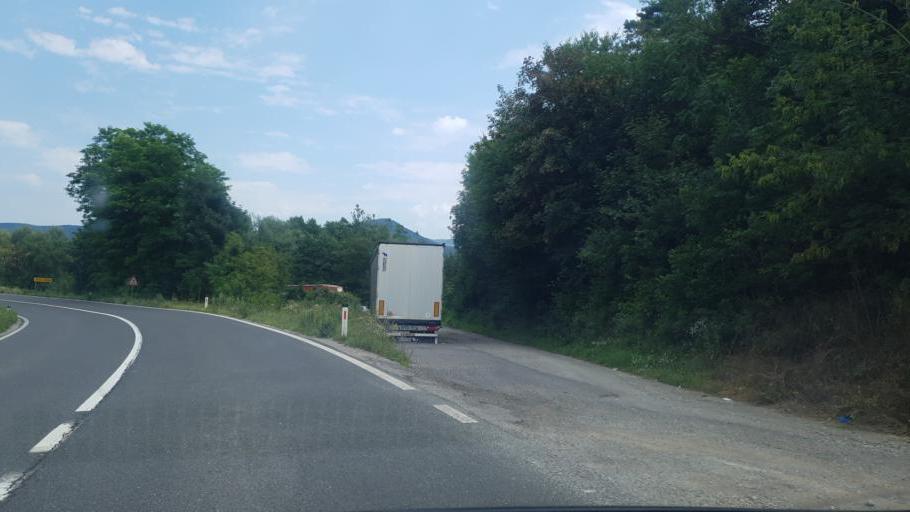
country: SI
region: Ilirska Bistrica
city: Ilirska Bistrica
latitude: 45.5382
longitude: 14.2499
